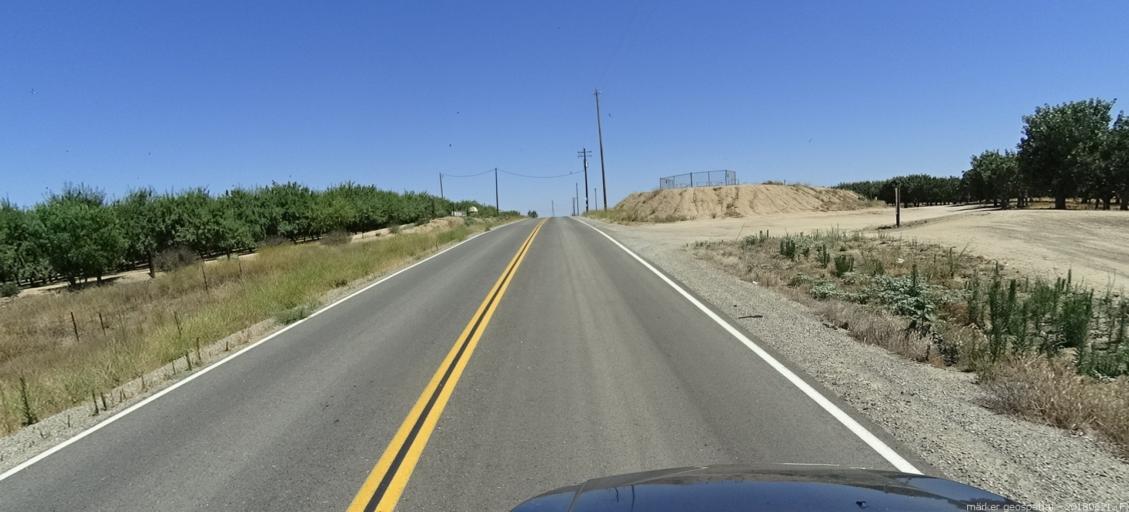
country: US
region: California
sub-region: Madera County
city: Bonadelle Ranchos-Madera Ranchos
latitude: 36.9070
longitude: -119.8940
